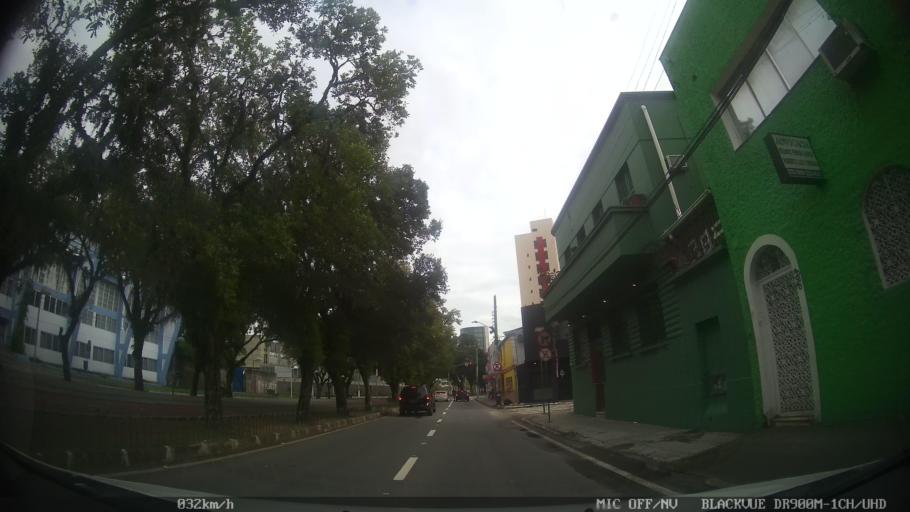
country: BR
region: Santa Catarina
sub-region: Florianopolis
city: Florianopolis
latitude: -27.5993
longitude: -48.5478
